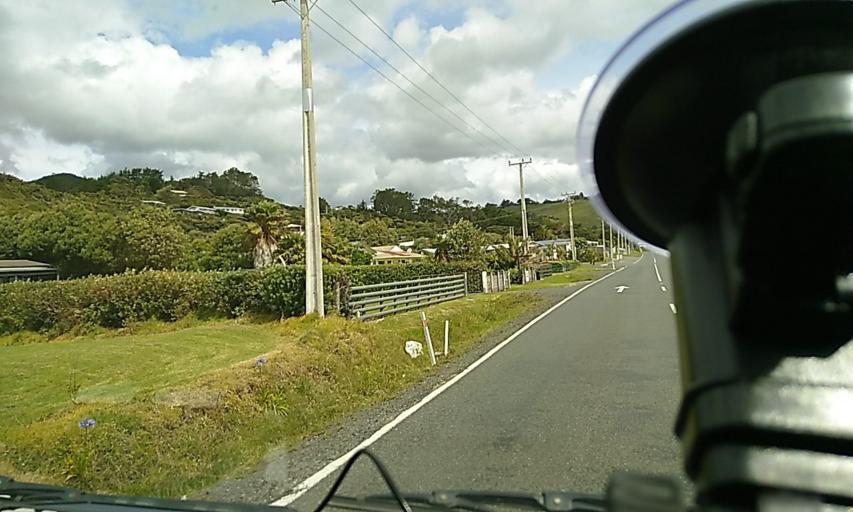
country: NZ
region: Northland
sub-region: Far North District
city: Ahipara
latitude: -35.5209
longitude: 173.3884
